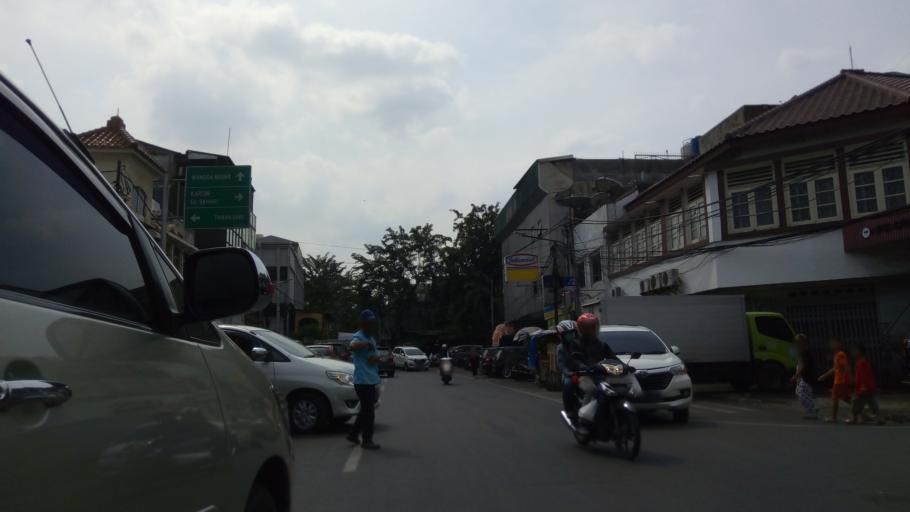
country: ID
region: Jakarta Raya
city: Jakarta
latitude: -6.1591
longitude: 106.8319
